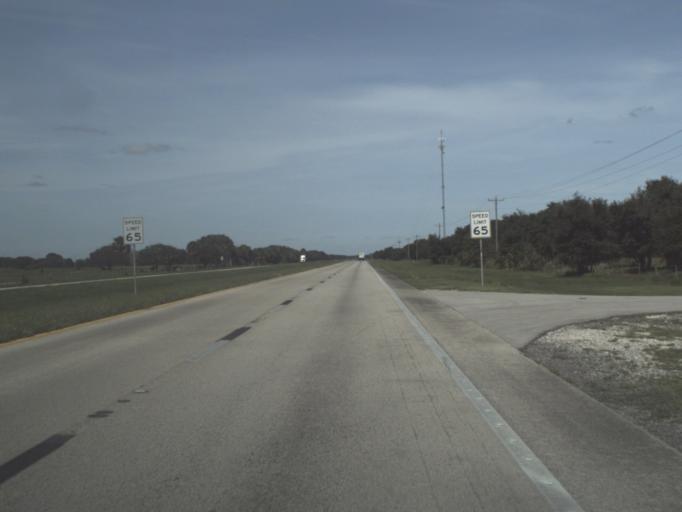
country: US
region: Florida
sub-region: Glades County
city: Moore Haven
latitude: 26.8632
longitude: -81.2135
